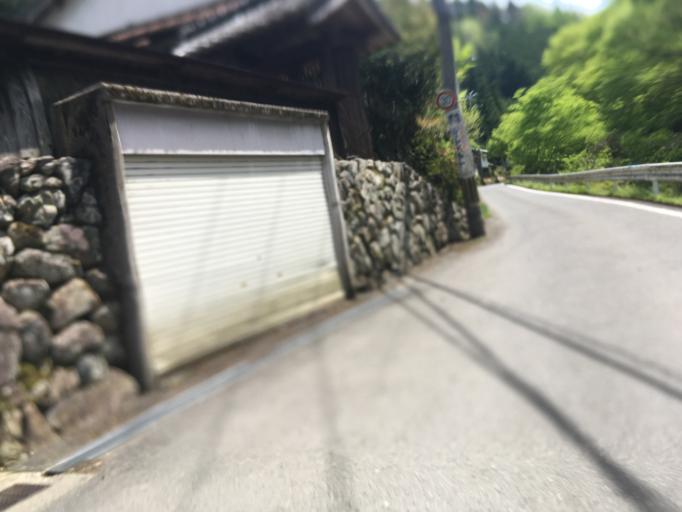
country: JP
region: Kyoto
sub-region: Kyoto-shi
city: Kamigyo-ku
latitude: 35.1111
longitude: 135.7240
